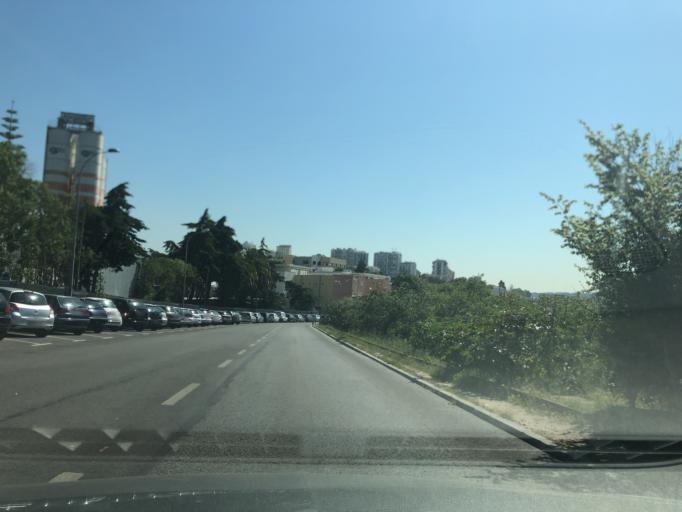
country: PT
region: Lisbon
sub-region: Oeiras
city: Carnaxide
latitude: 38.7345
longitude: -9.2346
